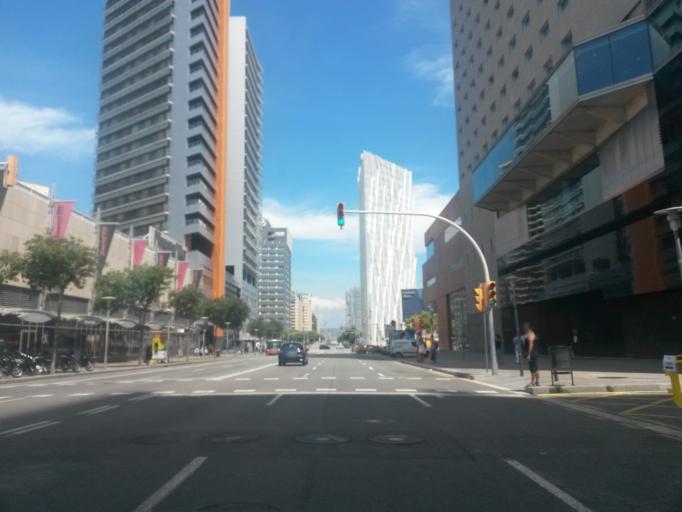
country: ES
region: Catalonia
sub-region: Provincia de Barcelona
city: Sant Marti
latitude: 41.4099
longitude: 2.2182
